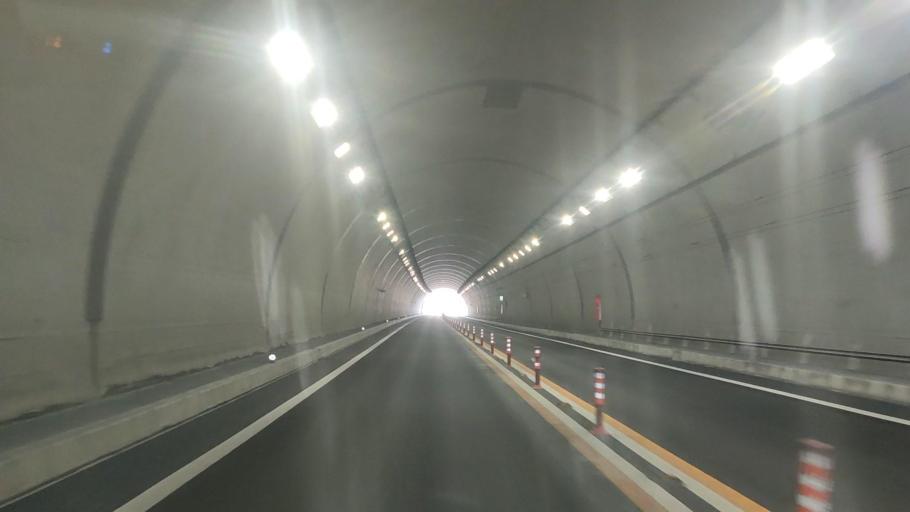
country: JP
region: Fukuoka
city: Yoshitomi
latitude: 33.5628
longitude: 131.1625
